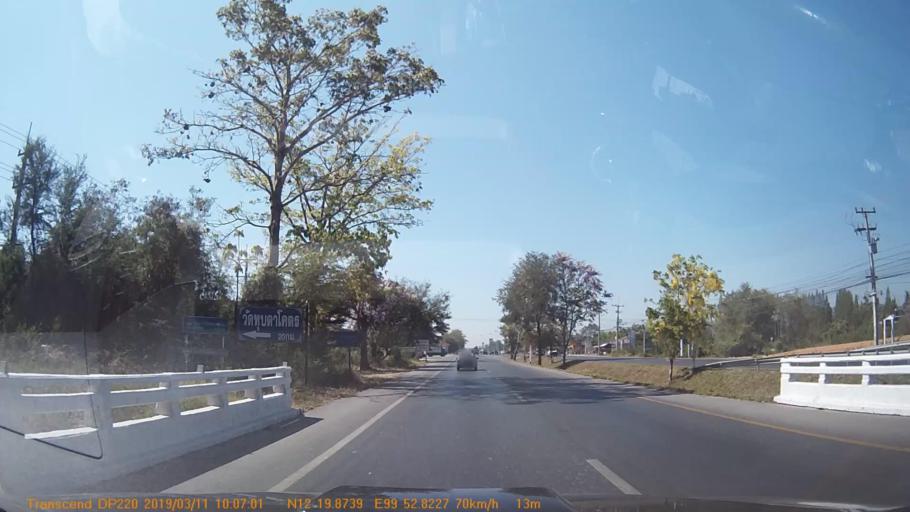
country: TH
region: Prachuap Khiri Khan
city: Pran Buri
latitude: 12.3309
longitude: 99.8803
